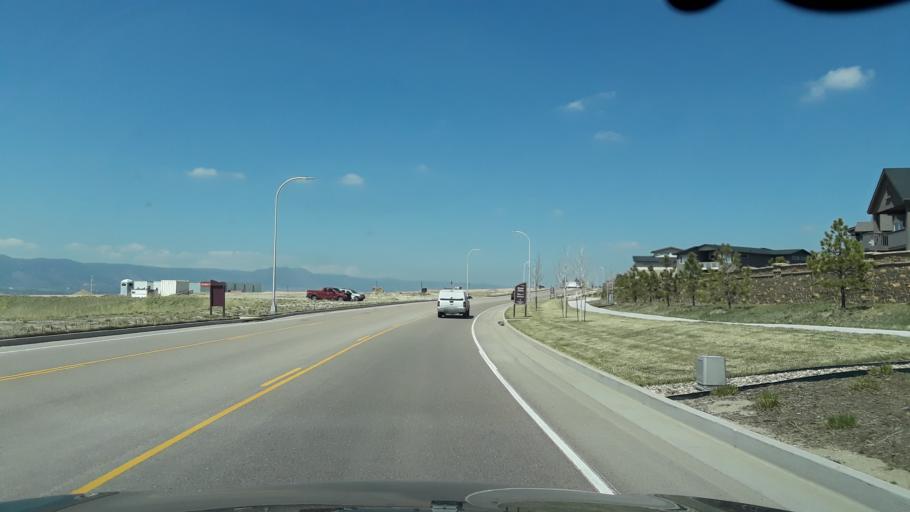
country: US
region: Colorado
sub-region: El Paso County
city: Black Forest
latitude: 38.9808
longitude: -104.7558
